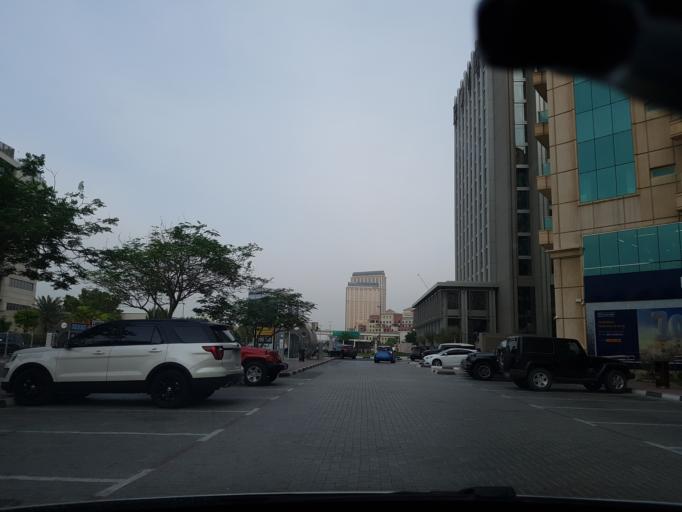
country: AE
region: Ash Shariqah
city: Sharjah
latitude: 25.2343
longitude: 55.3134
